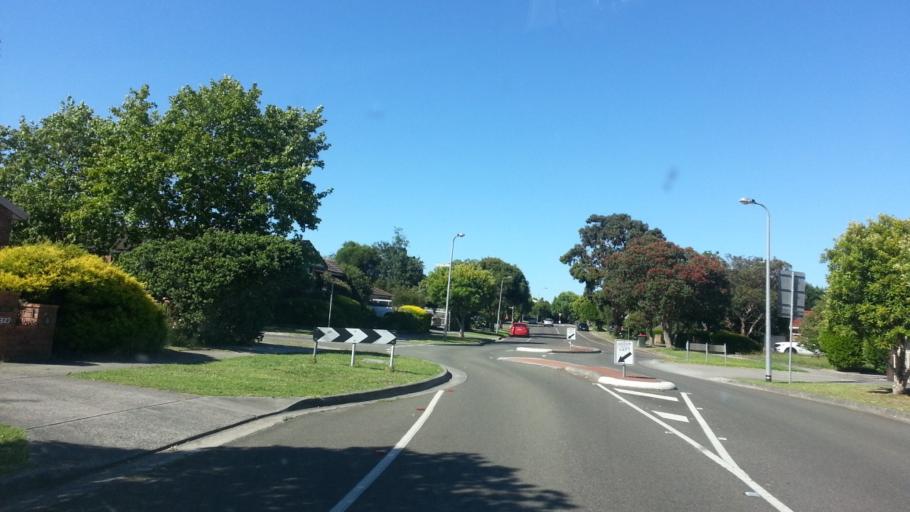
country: AU
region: Victoria
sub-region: Yarra Ranges
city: Lysterfield
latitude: -37.9244
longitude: 145.2669
